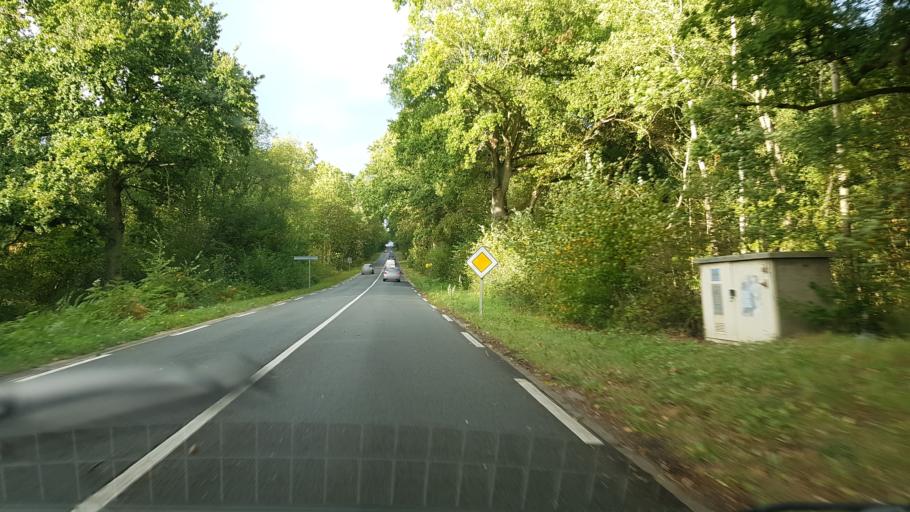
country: FR
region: Ile-de-France
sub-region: Departement de l'Essonne
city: Fontenay-les-Briis
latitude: 48.6248
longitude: 2.1733
